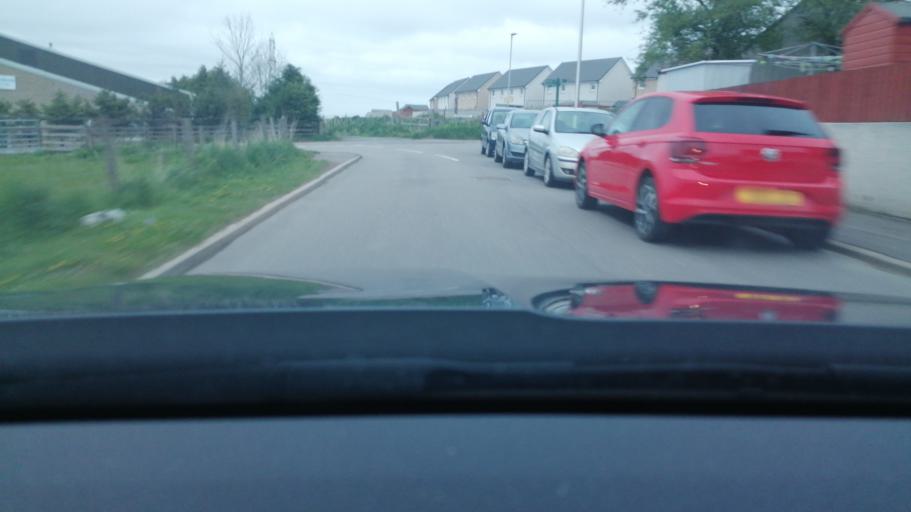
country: GB
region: Scotland
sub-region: Moray
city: Keith
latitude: 57.5363
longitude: -2.9435
